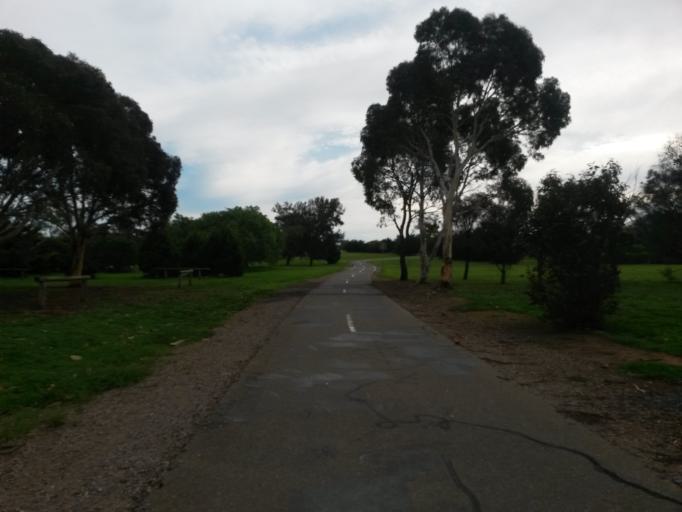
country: AU
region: South Australia
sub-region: Onkaparinga
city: Moana
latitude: -35.1983
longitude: 138.4884
